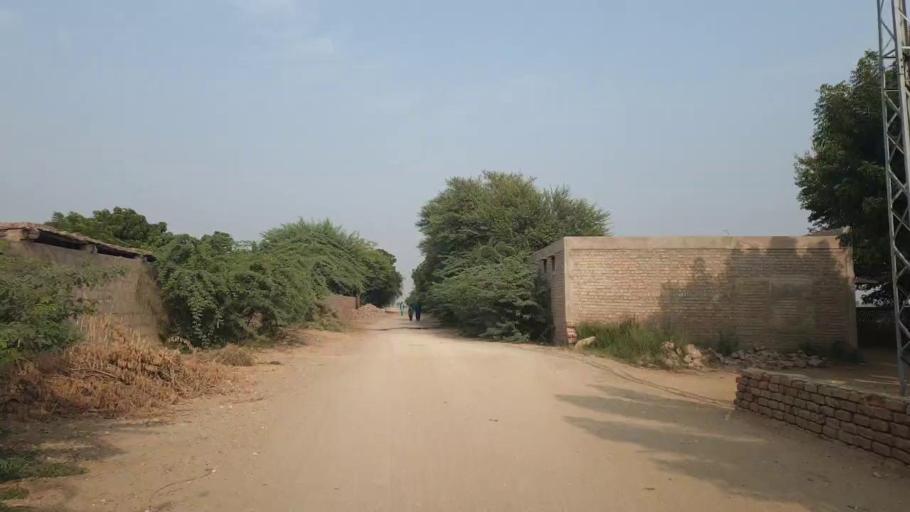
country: PK
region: Sindh
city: Sann
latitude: 26.0606
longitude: 68.1066
